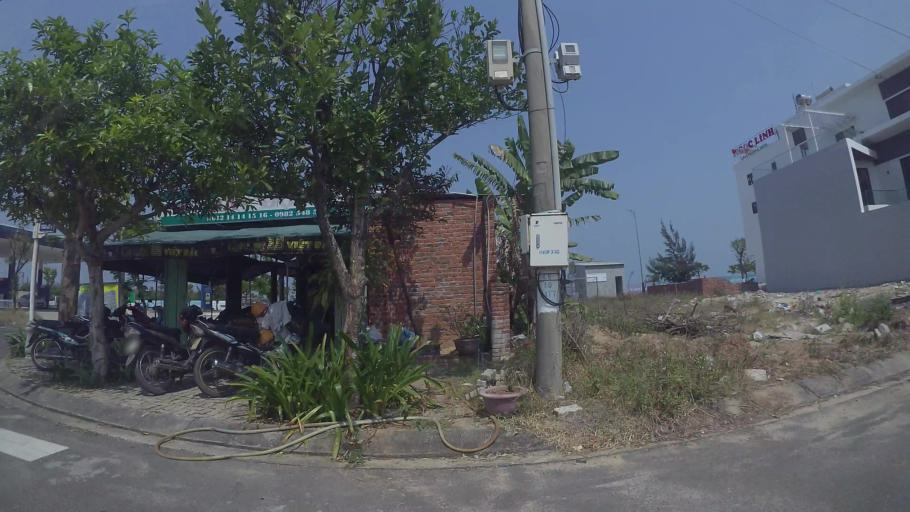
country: VN
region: Da Nang
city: Ngu Hanh Son
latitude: 15.9855
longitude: 108.2726
